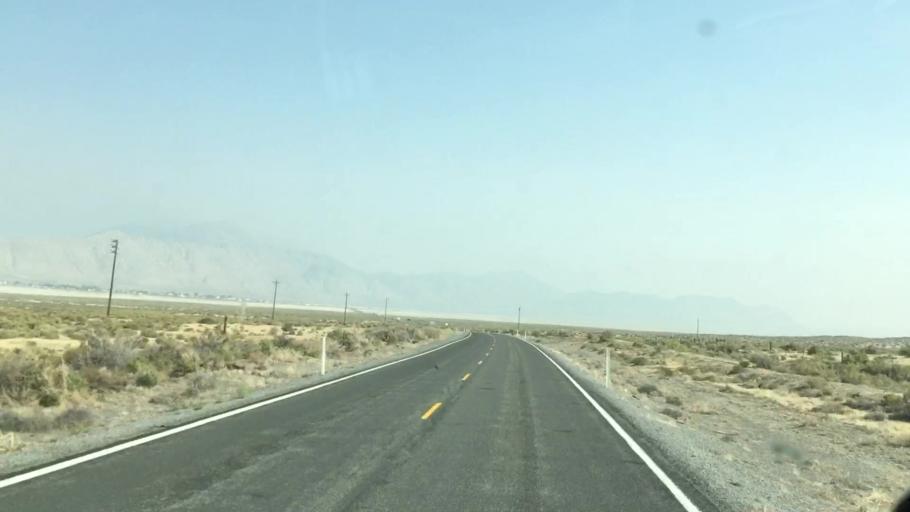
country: US
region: Nevada
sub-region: Pershing County
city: Lovelock
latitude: 40.6187
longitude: -119.3348
